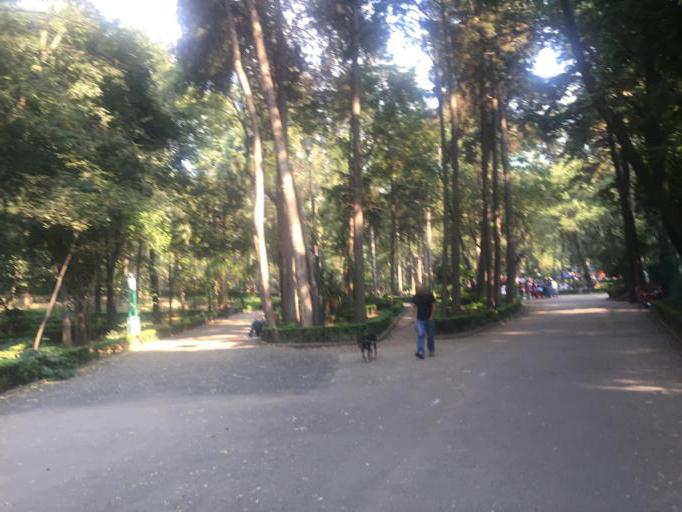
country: MX
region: Mexico City
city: Colonia del Valle
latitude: 19.3781
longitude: -99.1799
